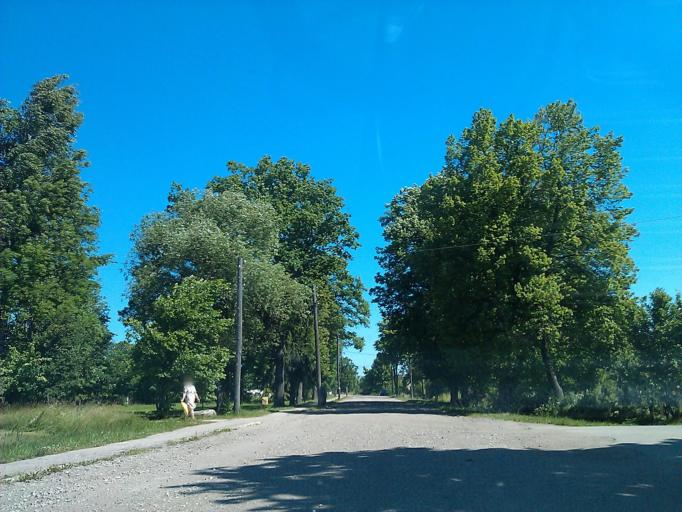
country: LV
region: Vilanu
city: Vilani
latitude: 56.5477
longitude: 26.9254
